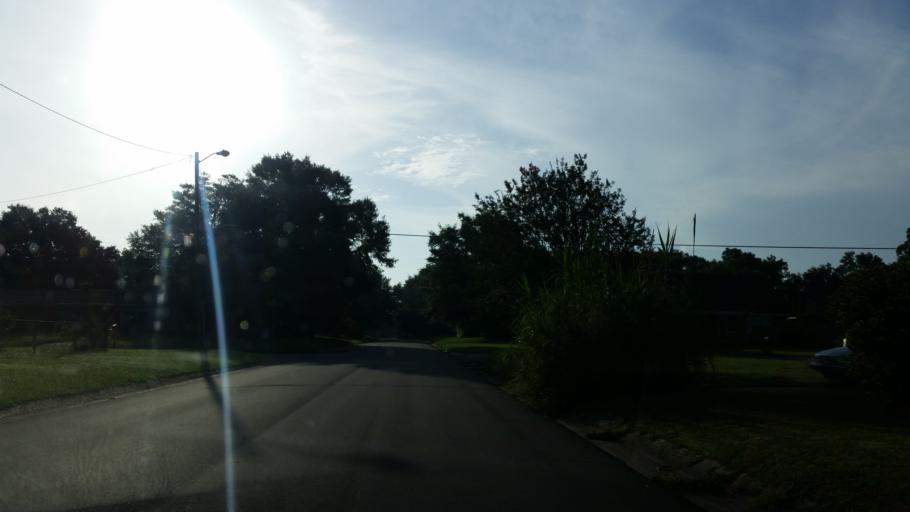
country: US
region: Florida
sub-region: Escambia County
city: Ferry Pass
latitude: 30.4899
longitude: -87.2006
